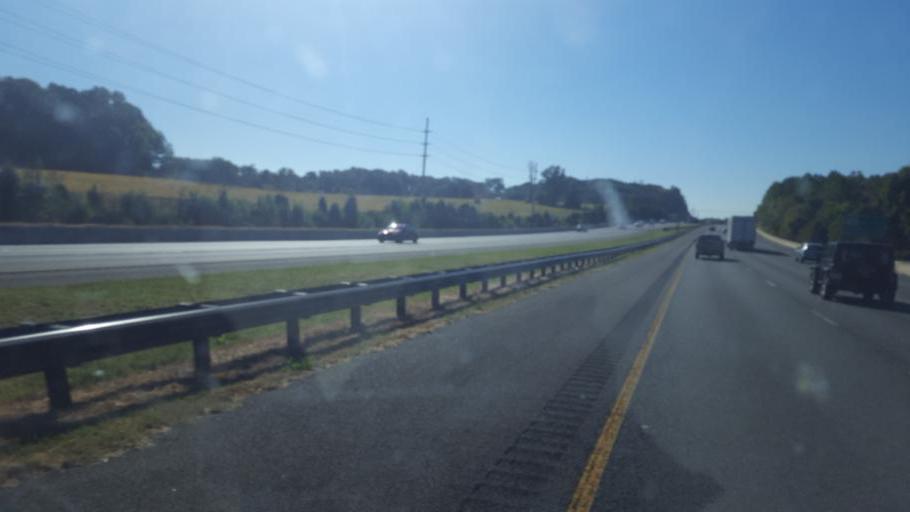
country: US
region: Maryland
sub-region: Montgomery County
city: Clarksburg
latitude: 39.2191
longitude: -77.2788
